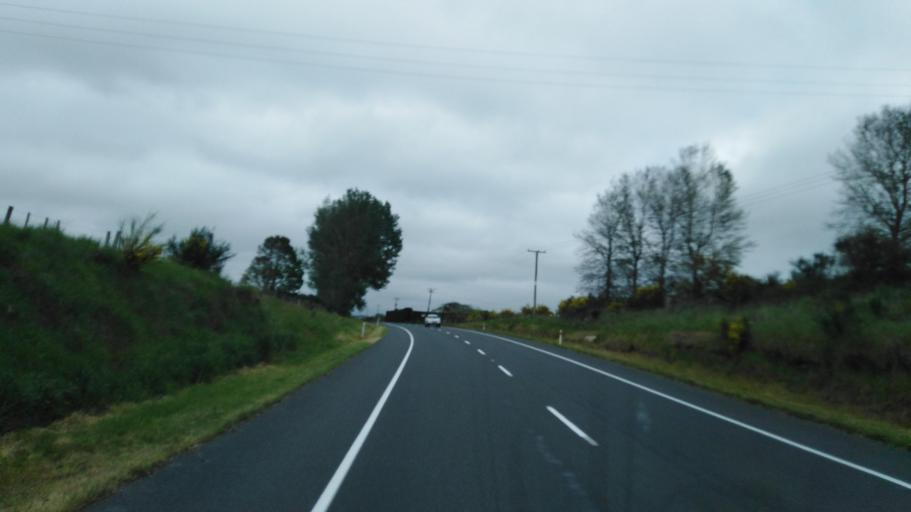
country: NZ
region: Waikato
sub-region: Taupo District
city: Taupo
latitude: -38.6117
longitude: 176.2718
